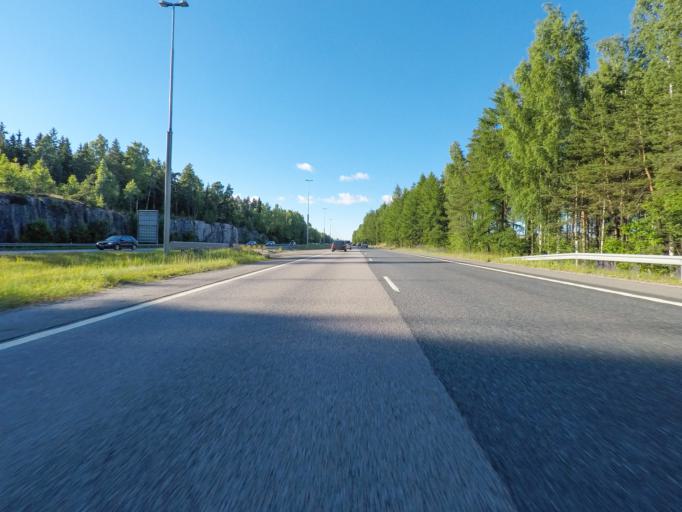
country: FI
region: Uusimaa
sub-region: Helsinki
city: Vantaa
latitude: 60.2856
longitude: 25.0936
